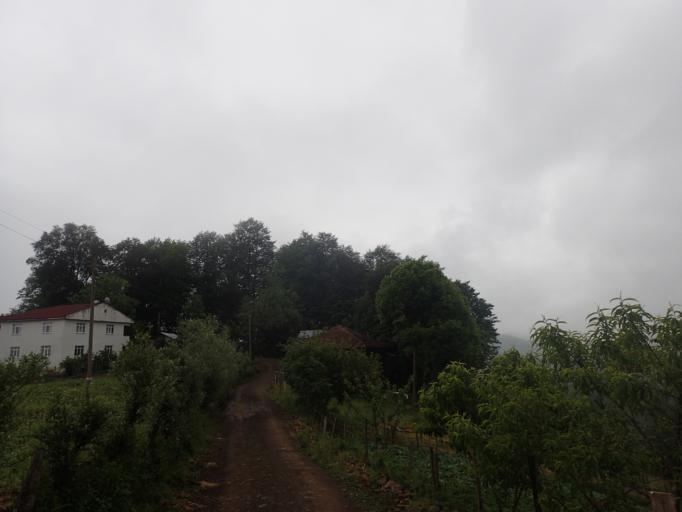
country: TR
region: Samsun
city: Salipazari
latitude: 40.9314
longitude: 36.8872
